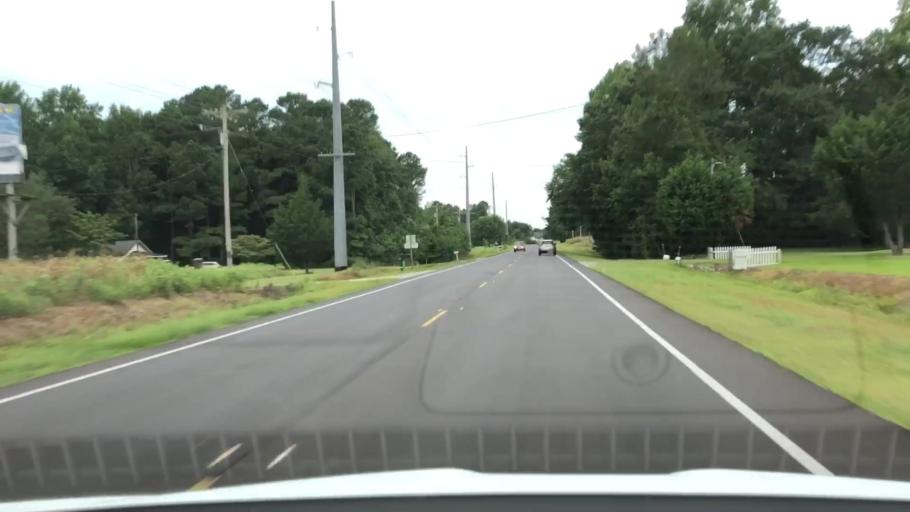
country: US
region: North Carolina
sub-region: Jones County
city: Maysville
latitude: 34.8335
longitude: -77.1648
